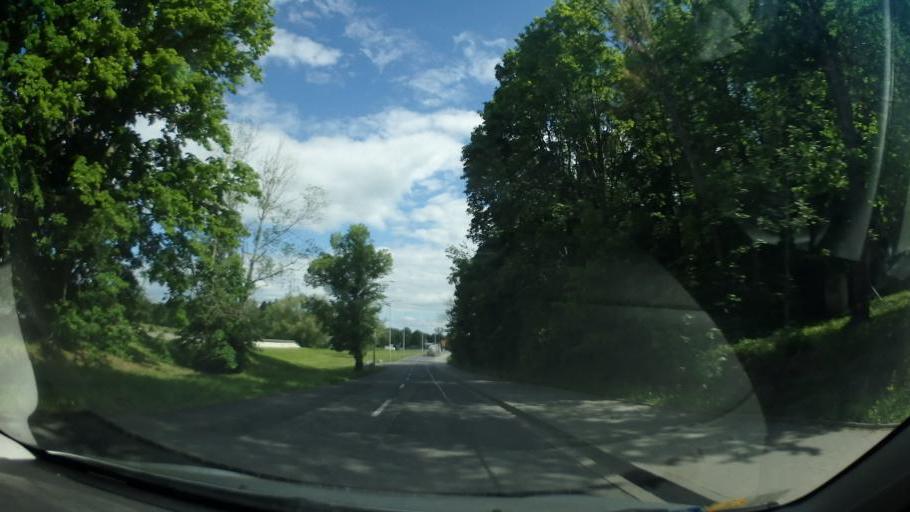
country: CZ
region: Pardubicky
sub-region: Okres Svitavy
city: Moravska Trebova
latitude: 49.7482
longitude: 16.6568
